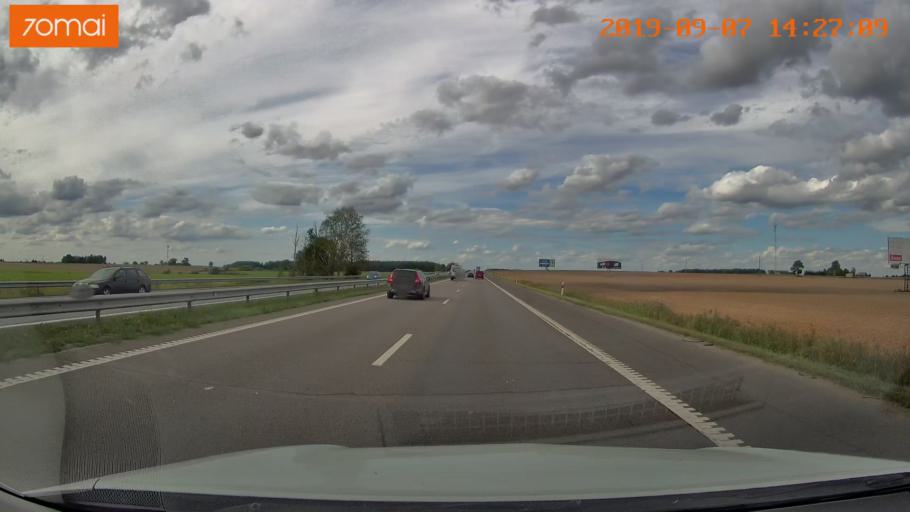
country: LT
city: Kaisiadorys
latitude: 54.8453
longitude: 24.3332
